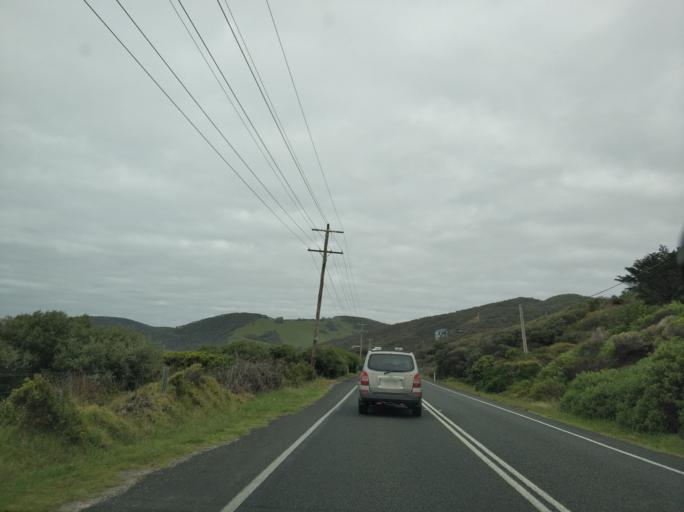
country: AU
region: Victoria
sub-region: Surf Coast
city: Anglesea
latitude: -38.4709
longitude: 144.0506
